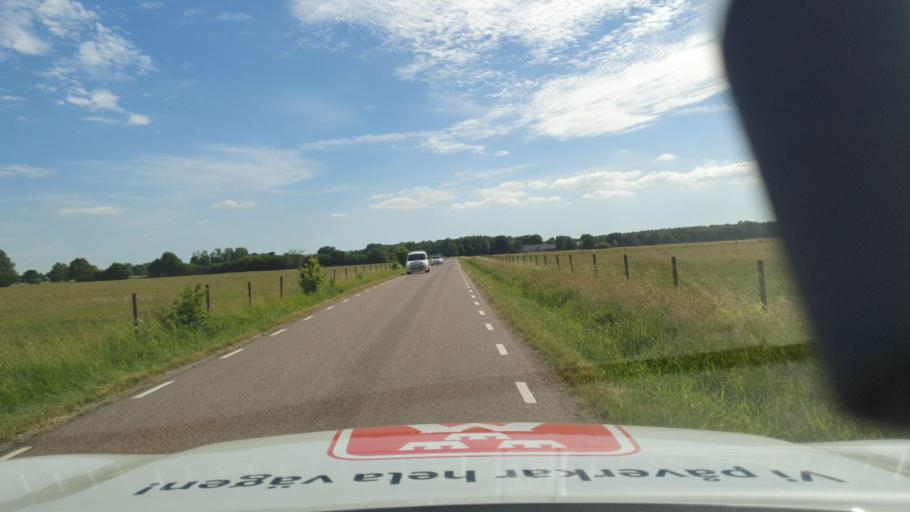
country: SE
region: Skane
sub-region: Sjobo Kommun
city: Blentarp
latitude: 55.6196
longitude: 13.6234
